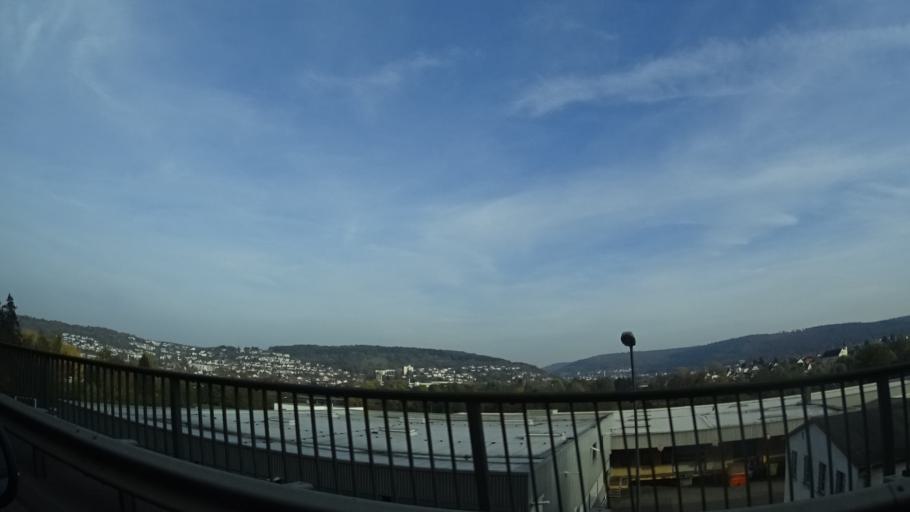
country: DE
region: Baden-Wuerttemberg
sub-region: Karlsruhe Region
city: Obrigheim
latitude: 49.3433
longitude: 9.0963
